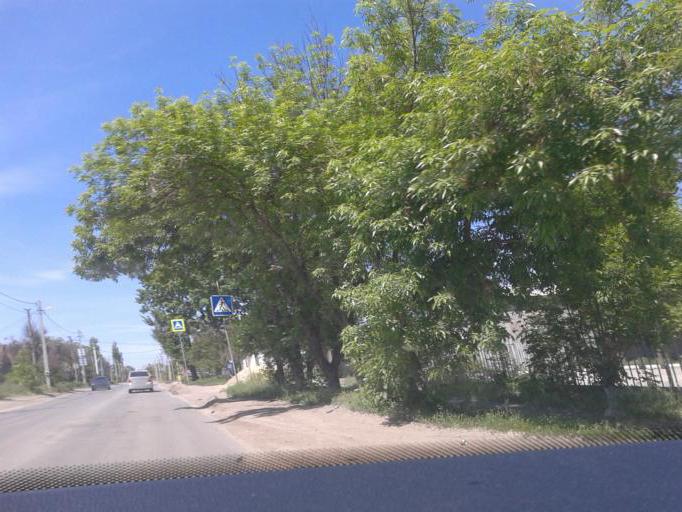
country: RU
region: Volgograd
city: Volgograd
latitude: 48.7512
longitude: 44.5403
